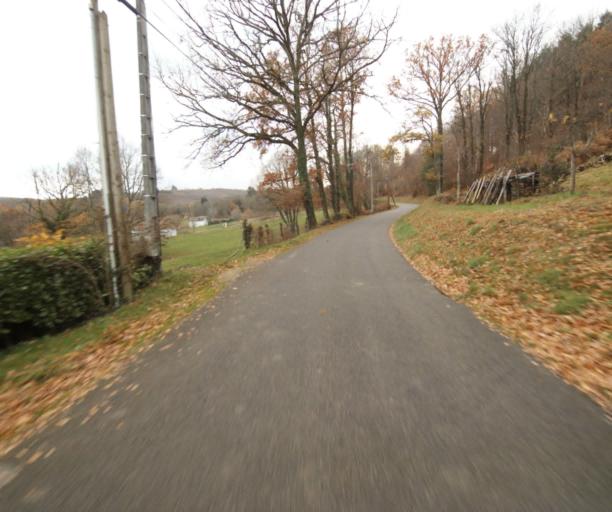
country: FR
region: Limousin
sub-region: Departement de la Correze
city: Sainte-Fortunade
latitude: 45.2170
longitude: 1.7825
